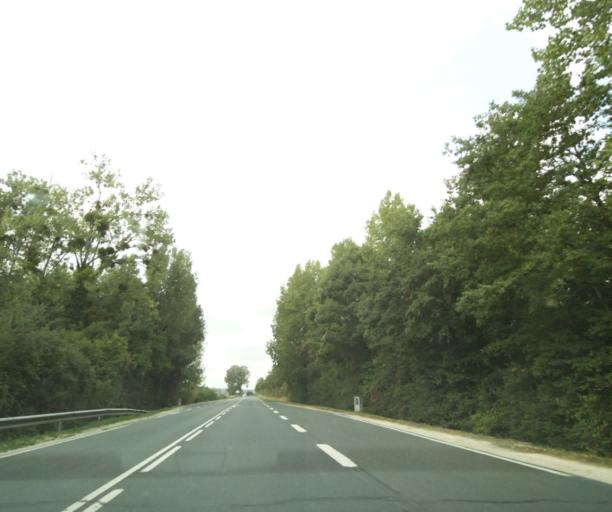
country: FR
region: Centre
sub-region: Departement de l'Indre
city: Buzancais
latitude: 46.8858
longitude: 1.4065
